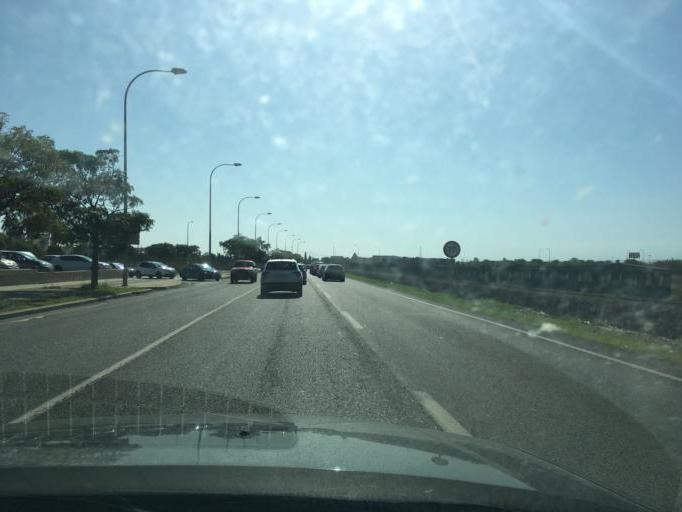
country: ES
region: Balearic Islands
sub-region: Illes Balears
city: Palma
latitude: 39.5734
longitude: 2.6854
